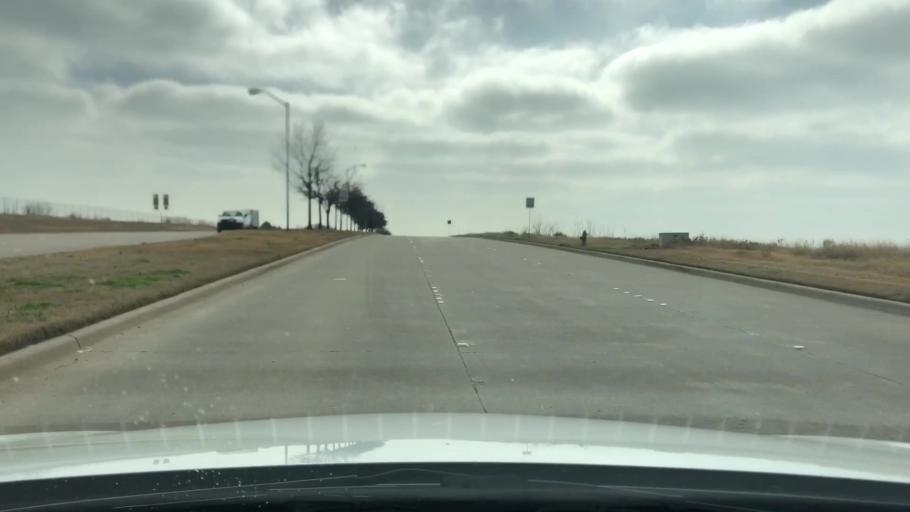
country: US
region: Texas
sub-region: Denton County
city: The Colony
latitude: 33.0799
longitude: -96.8510
